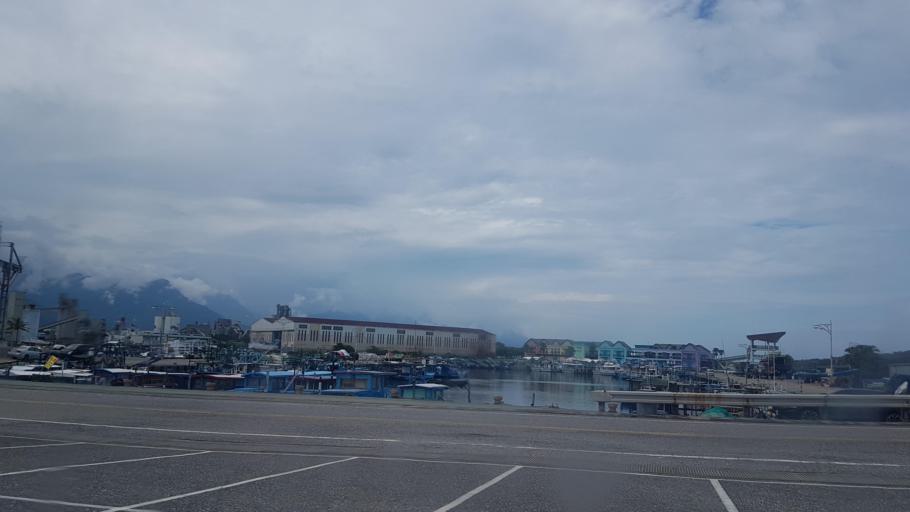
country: TW
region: Taiwan
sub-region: Hualien
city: Hualian
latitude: 23.9957
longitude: 121.6395
